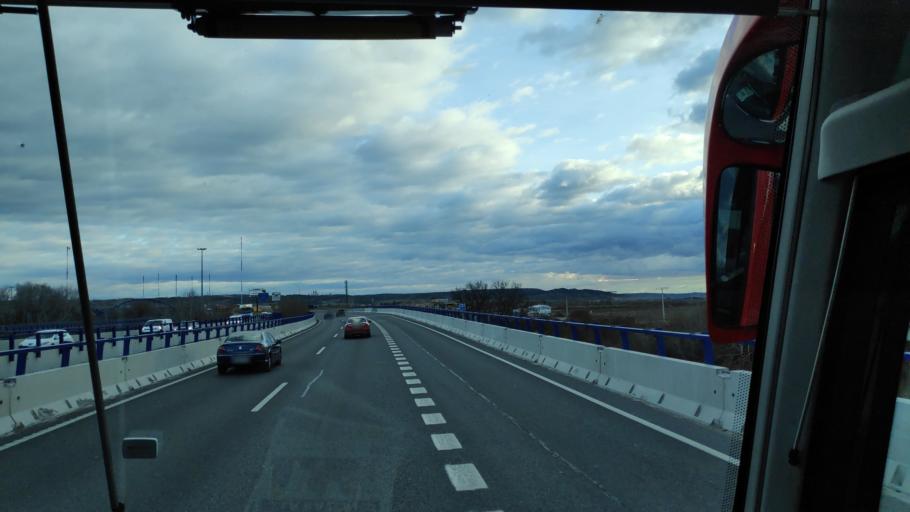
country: ES
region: Madrid
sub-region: Provincia de Madrid
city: Vaciamadrid
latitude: 40.3215
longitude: -3.5157
